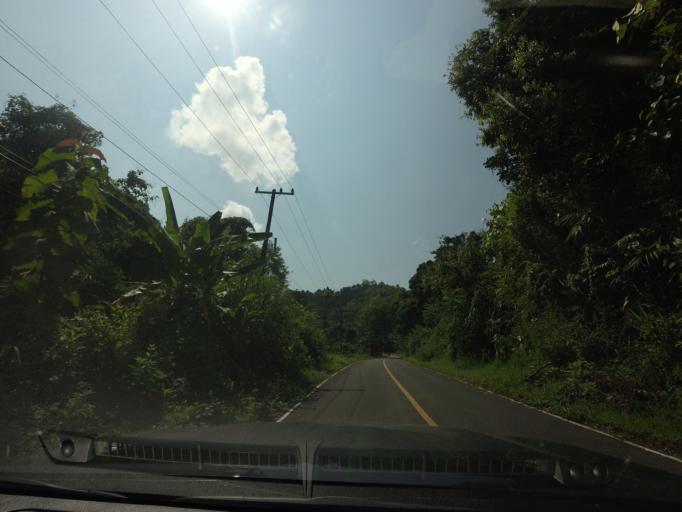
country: TH
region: Nan
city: Bo Kluea
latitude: 19.0525
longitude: 101.1671
